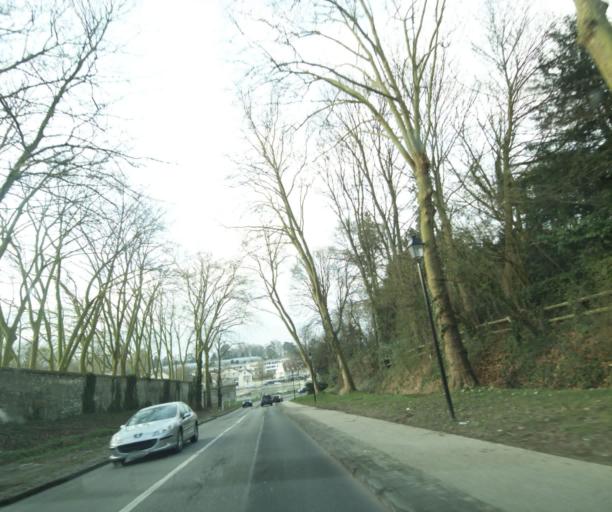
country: FR
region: Ile-de-France
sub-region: Departement des Yvelines
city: Louveciennes
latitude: 48.8654
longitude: 2.1026
